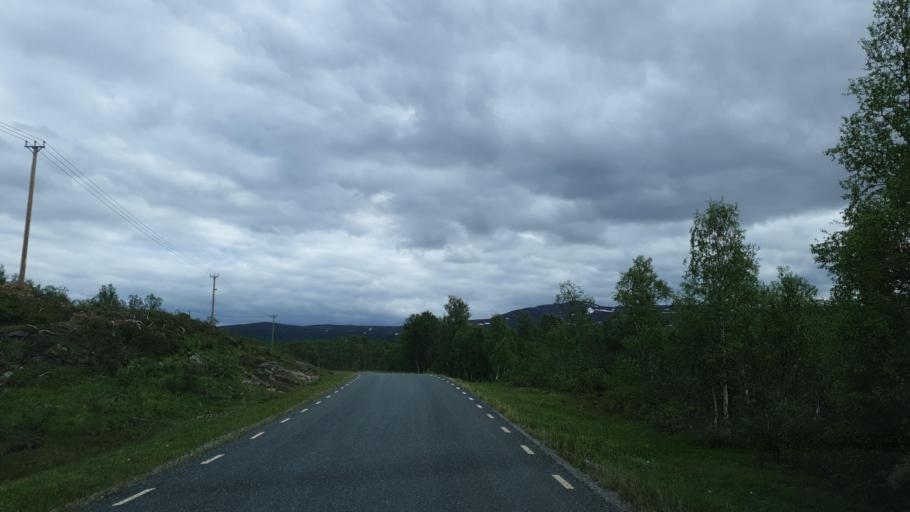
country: NO
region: Nordland
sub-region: Hattfjelldal
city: Hattfjelldal
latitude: 65.4201
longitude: 14.6765
